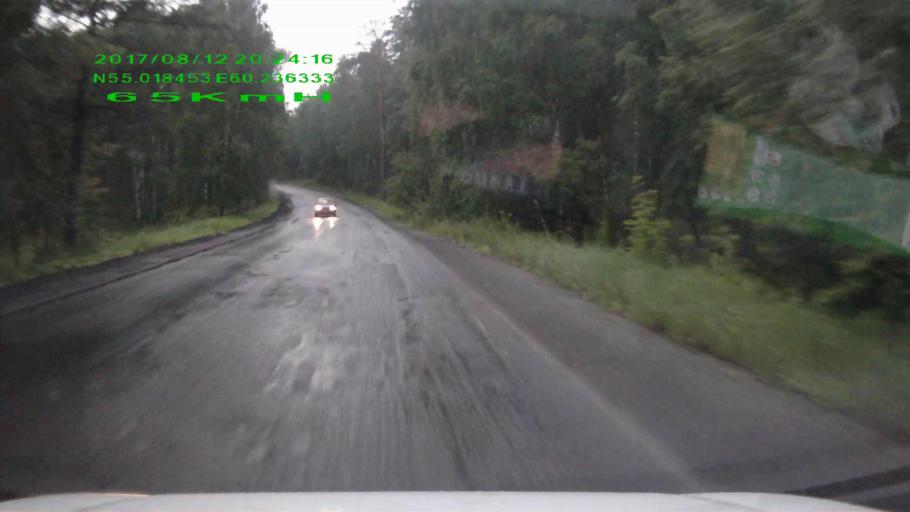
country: RU
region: Chelyabinsk
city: Miass
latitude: 55.0183
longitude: 60.2360
